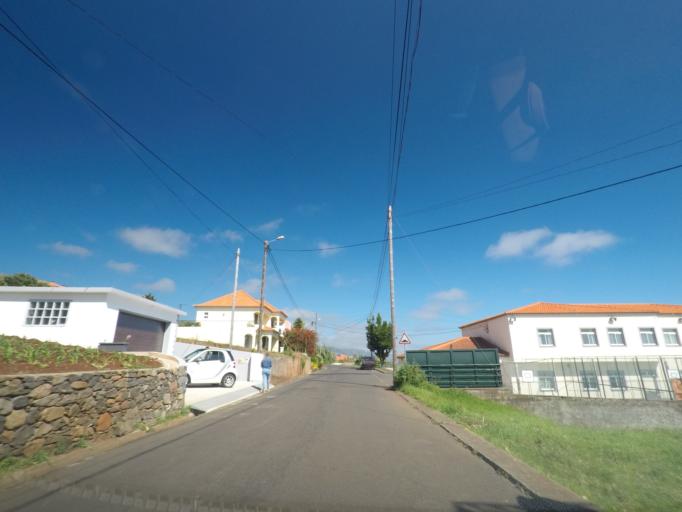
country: PT
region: Madeira
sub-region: Calheta
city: Arco da Calheta
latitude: 32.7005
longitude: -17.1195
